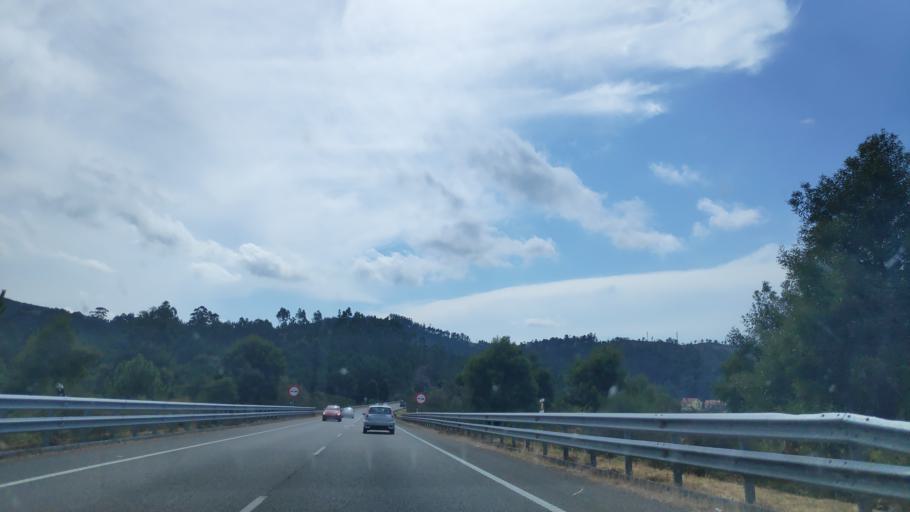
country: ES
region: Galicia
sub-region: Provincia de Pontevedra
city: Vilagarcia de Arousa
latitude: 42.6044
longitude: -8.7337
